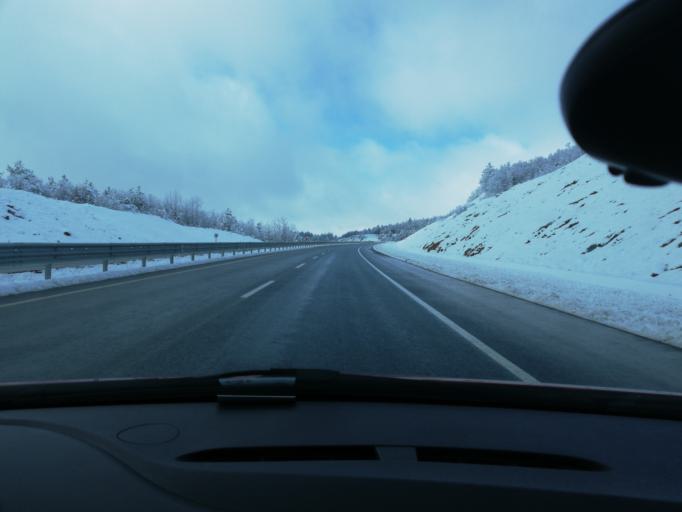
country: TR
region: Kastamonu
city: Ihsangazi
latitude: 41.3250
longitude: 33.6125
